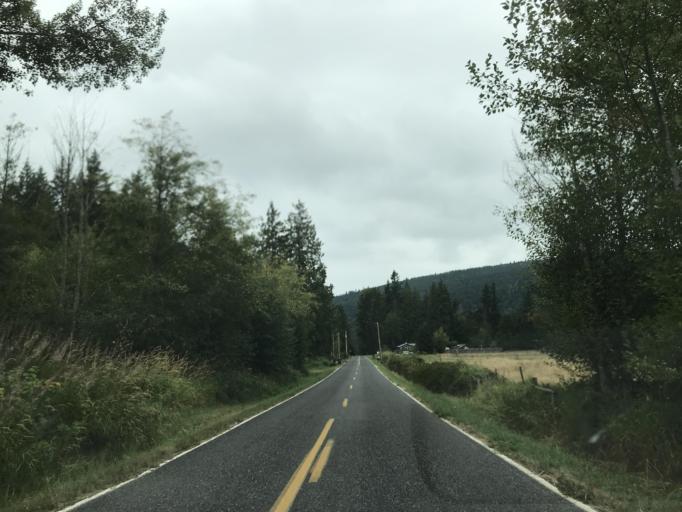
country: US
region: Washington
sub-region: Whatcom County
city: Sudden Valley
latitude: 48.7749
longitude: -122.3385
